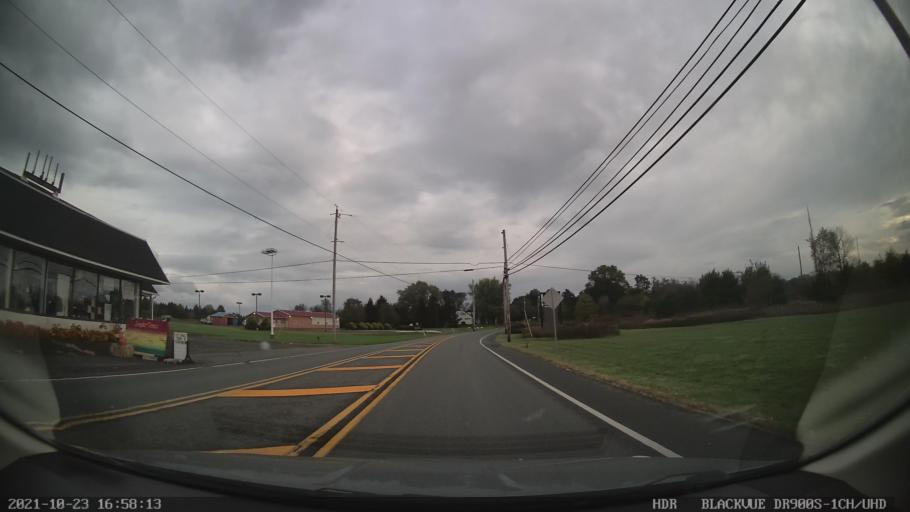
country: US
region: Pennsylvania
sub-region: Berks County
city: Bally
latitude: 40.4384
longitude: -75.5466
